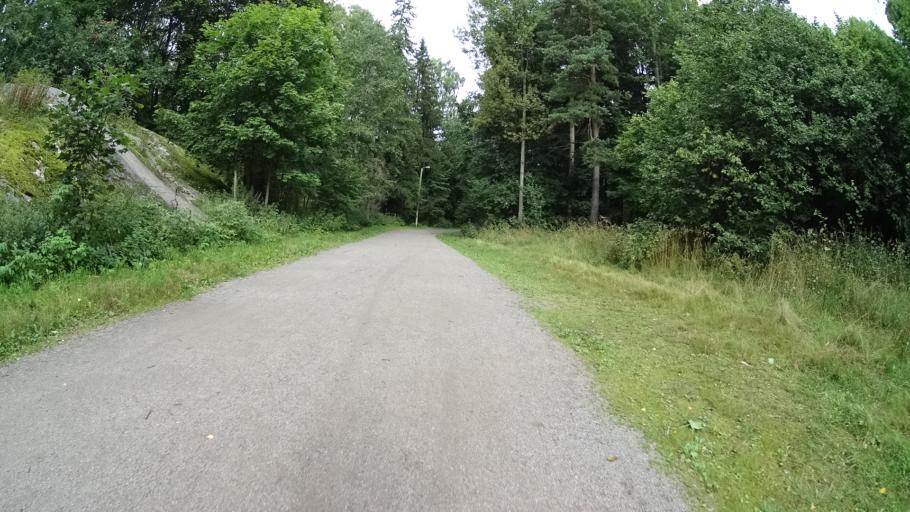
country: FI
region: Uusimaa
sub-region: Helsinki
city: Helsinki
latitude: 60.2291
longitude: 24.9822
